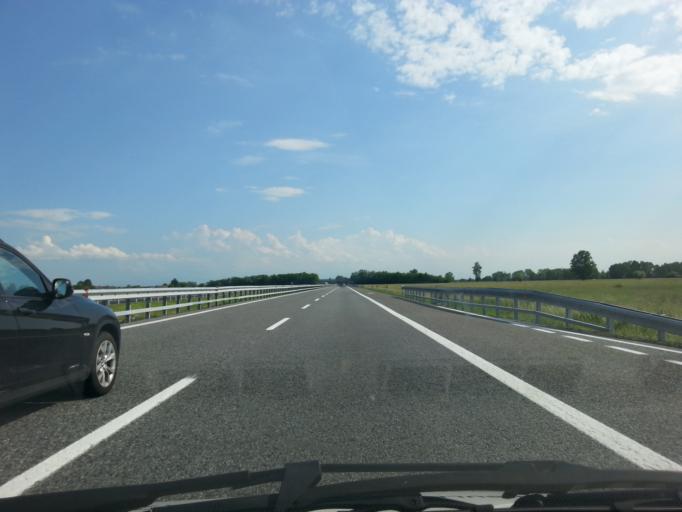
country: IT
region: Piedmont
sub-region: Provincia di Cuneo
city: Caramagna Piemonte
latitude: 44.7642
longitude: 7.7507
